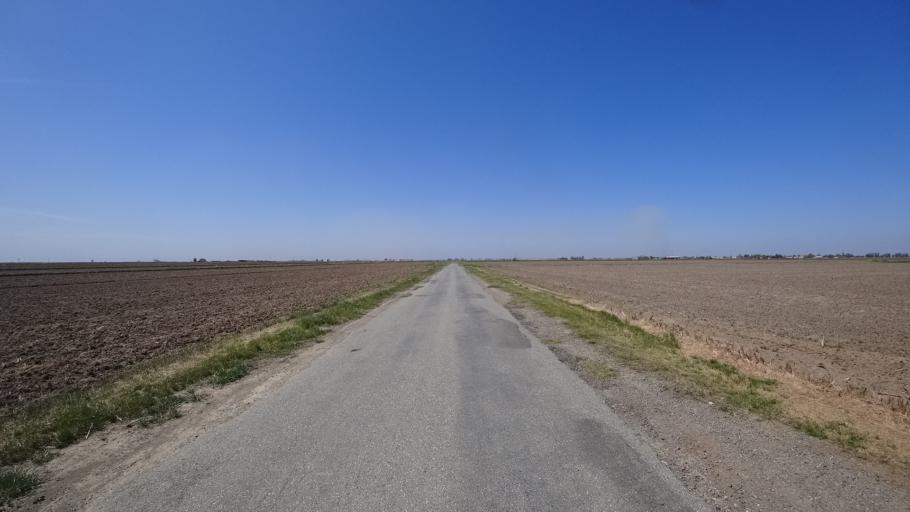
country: US
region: California
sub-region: Glenn County
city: Willows
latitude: 39.5654
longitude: -122.0217
